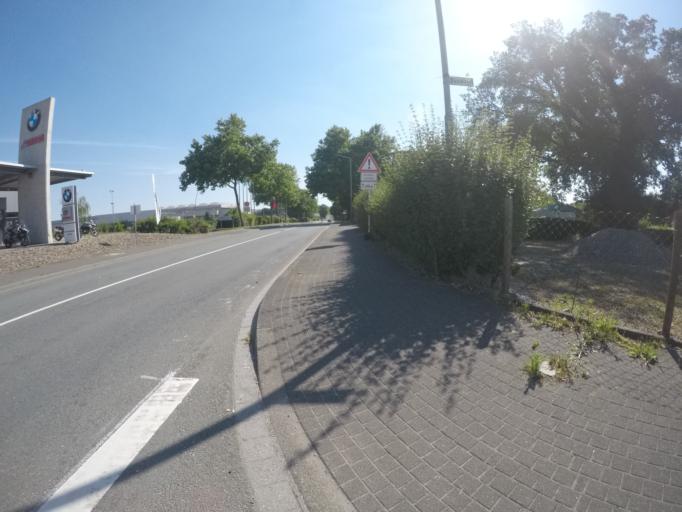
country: DE
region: North Rhine-Westphalia
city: Bad Oeynhausen
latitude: 52.1801
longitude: 8.7535
